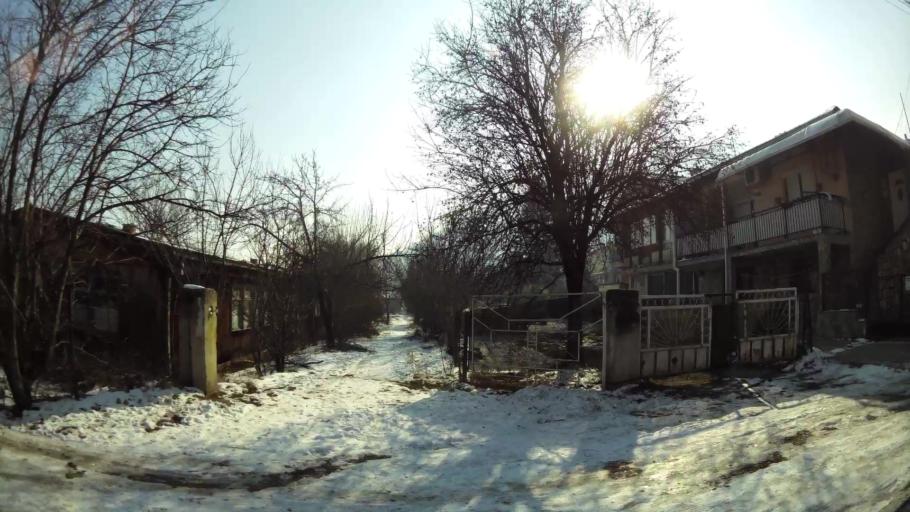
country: MK
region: Karpos
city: Skopje
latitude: 41.9754
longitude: 21.4341
